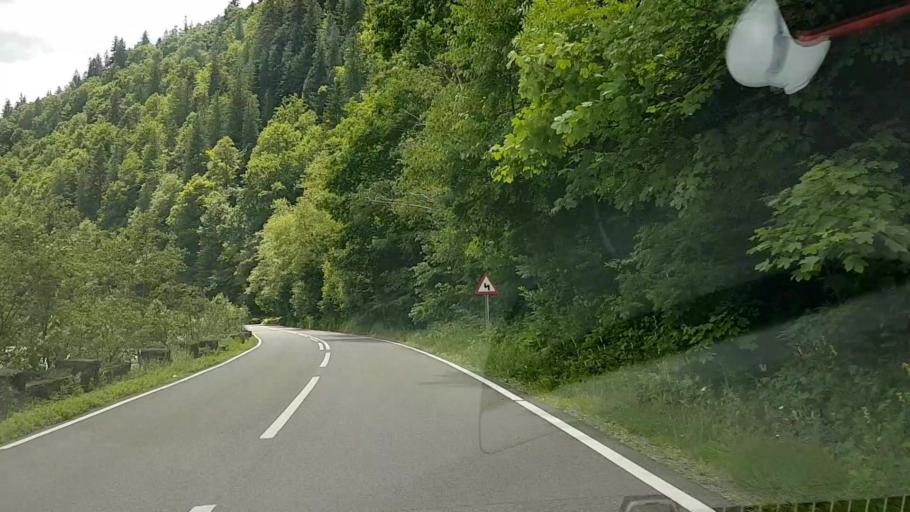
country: RO
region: Suceava
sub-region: Comuna Crucea
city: Crucea
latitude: 47.3162
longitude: 25.6253
